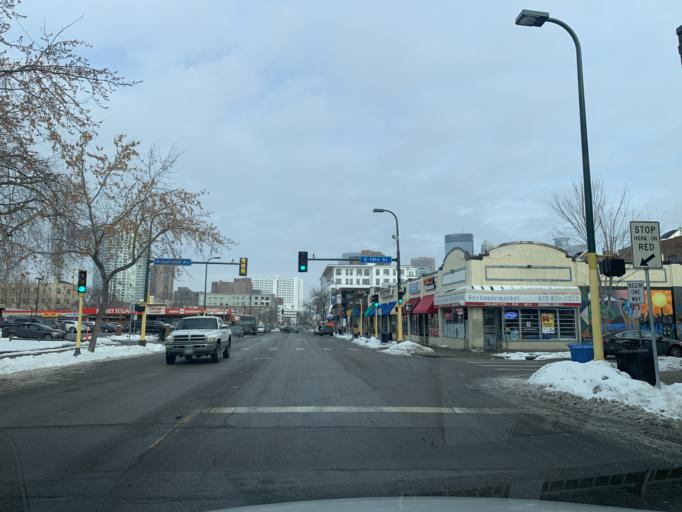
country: US
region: Minnesota
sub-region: Hennepin County
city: Minneapolis
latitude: 44.9637
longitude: -93.2778
